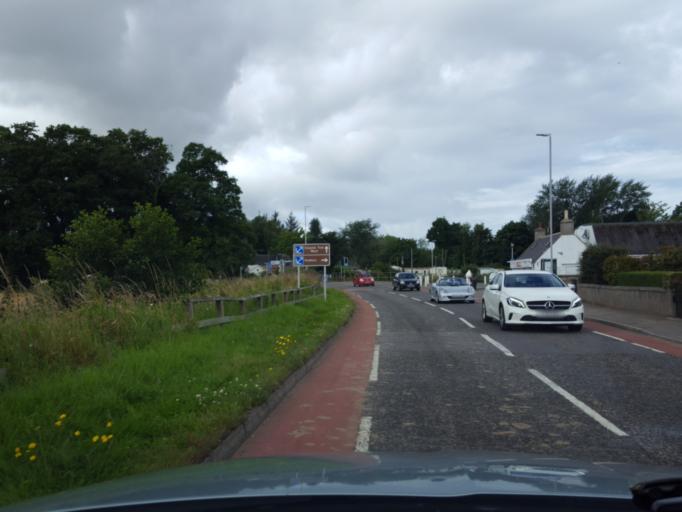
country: GB
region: Scotland
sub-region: Moray
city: Kinloss
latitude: 57.6347
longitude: -3.5688
